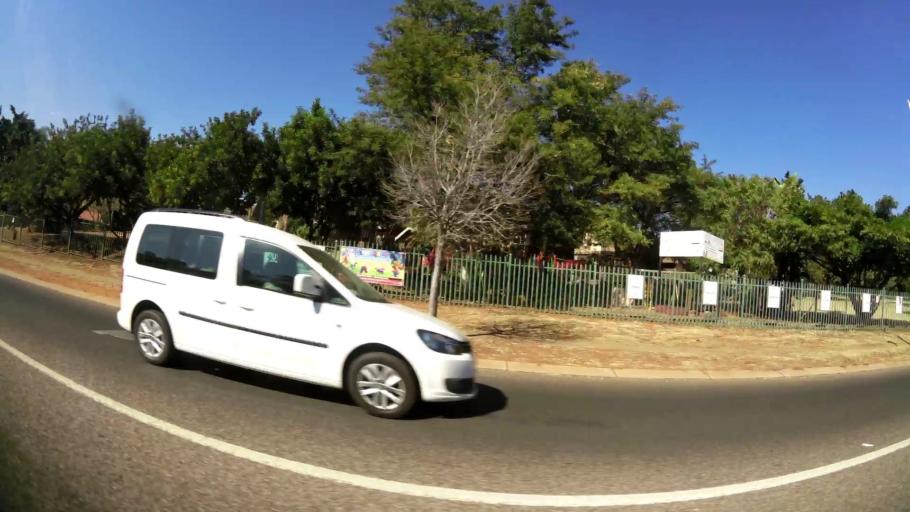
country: ZA
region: Gauteng
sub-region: City of Tshwane Metropolitan Municipality
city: Pretoria
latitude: -25.6869
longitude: 28.2368
